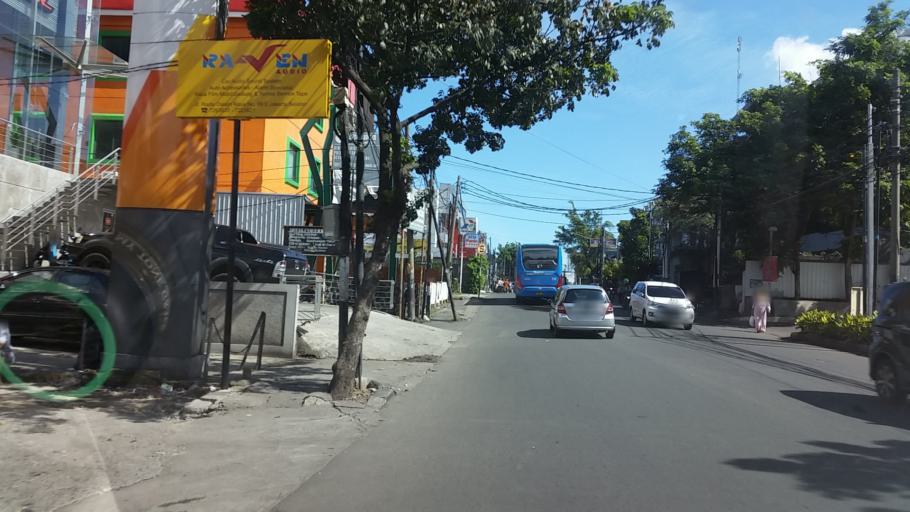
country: ID
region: Jakarta Raya
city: Jakarta
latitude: -6.2605
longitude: 106.7890
